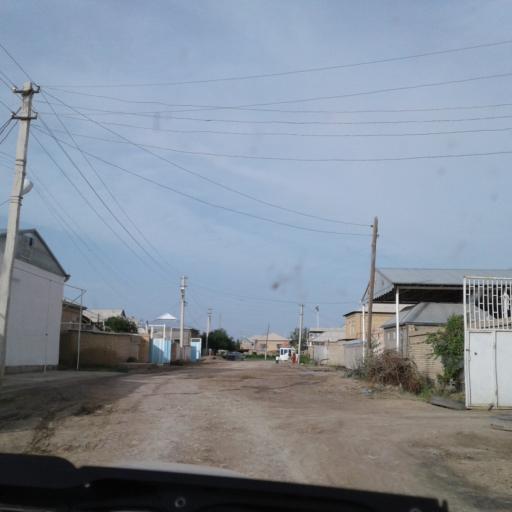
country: TM
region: Mary
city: Mary
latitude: 37.5810
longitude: 61.8745
